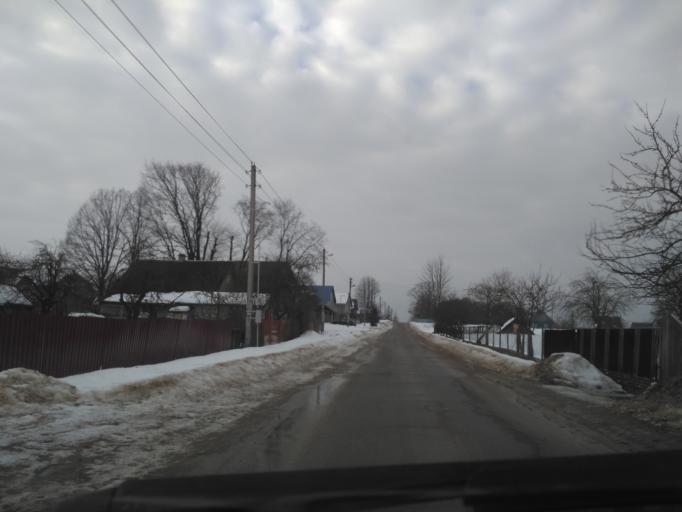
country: BY
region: Minsk
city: Zamostochcha
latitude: 53.8902
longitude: 27.9114
